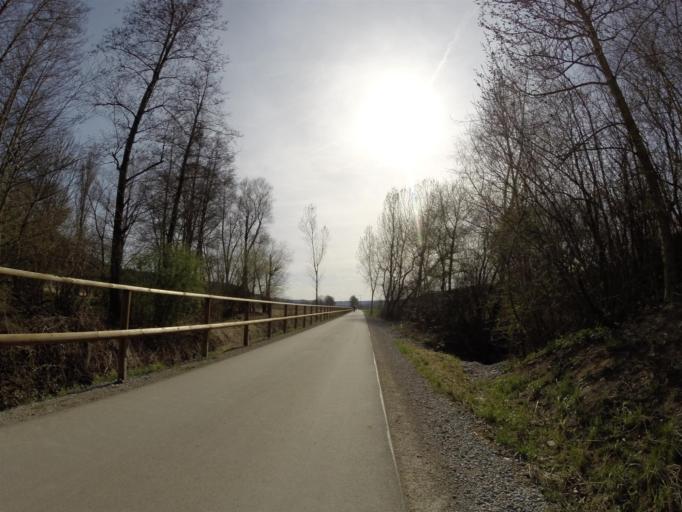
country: DE
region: Thuringia
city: Neuengonna
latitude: 50.9739
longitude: 11.6435
